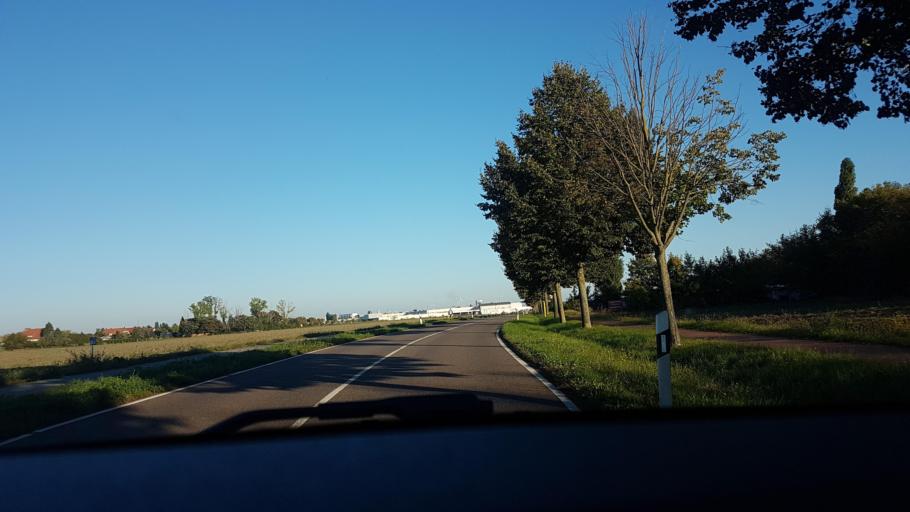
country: DE
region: Saxony-Anhalt
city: Bernburg
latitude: 51.7787
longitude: 11.7263
